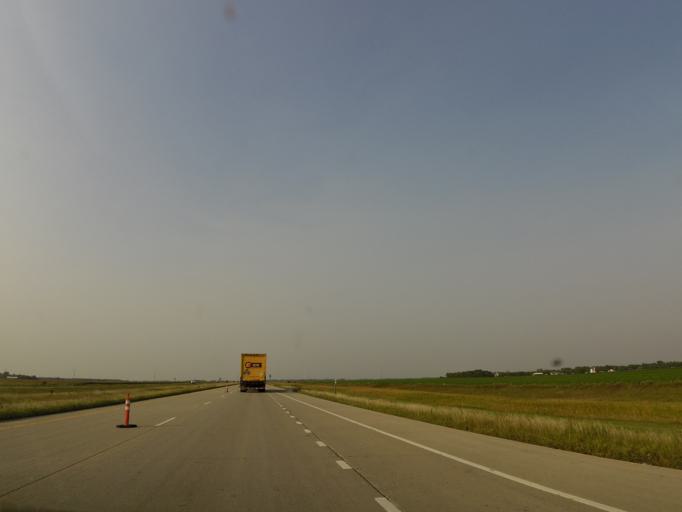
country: US
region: North Dakota
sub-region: Cass County
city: Horace
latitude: 46.6641
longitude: -96.8310
